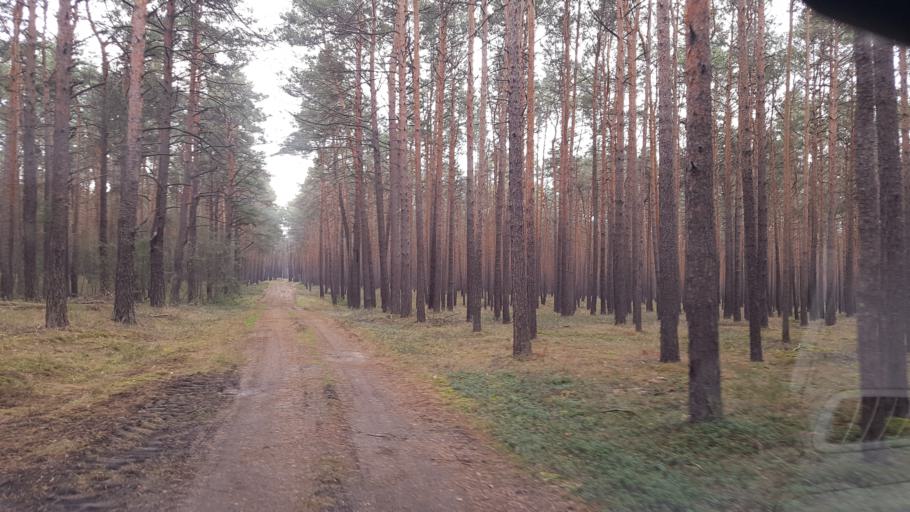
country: DE
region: Brandenburg
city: Schonborn
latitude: 51.6589
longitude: 13.4709
